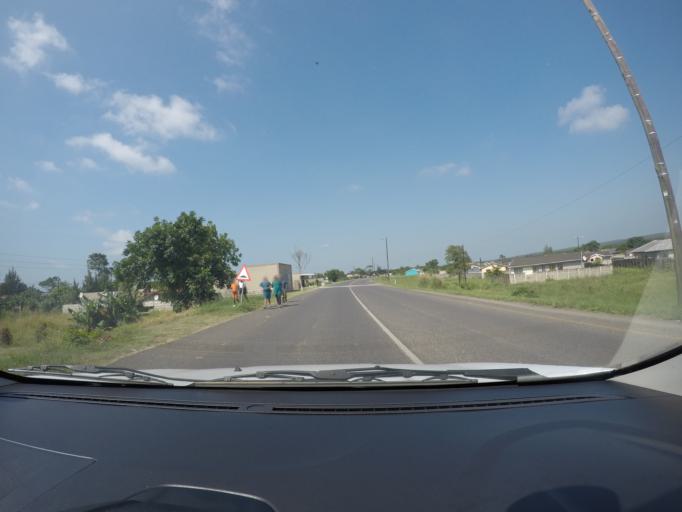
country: ZA
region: KwaZulu-Natal
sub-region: uThungulu District Municipality
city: eSikhawini
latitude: -28.8911
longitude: 31.8918
